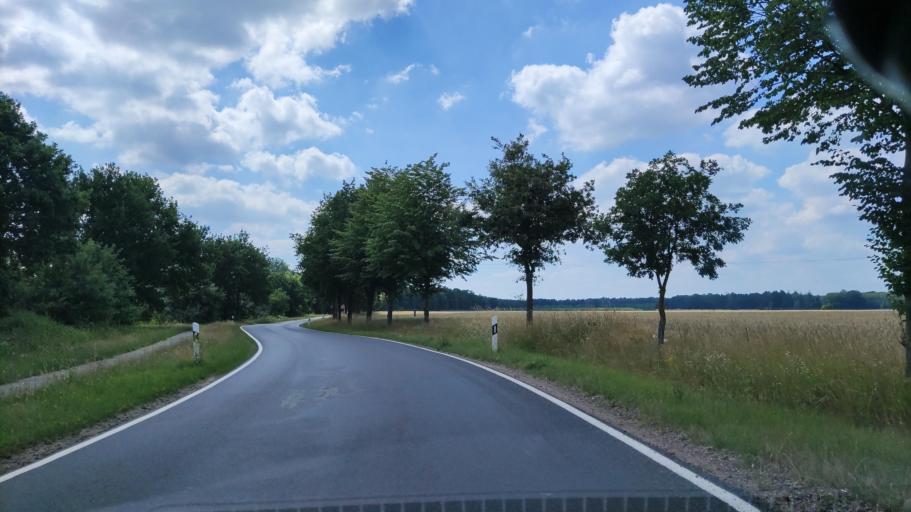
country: DE
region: Mecklenburg-Vorpommern
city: Lubtheen
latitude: 53.3368
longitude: 11.1357
